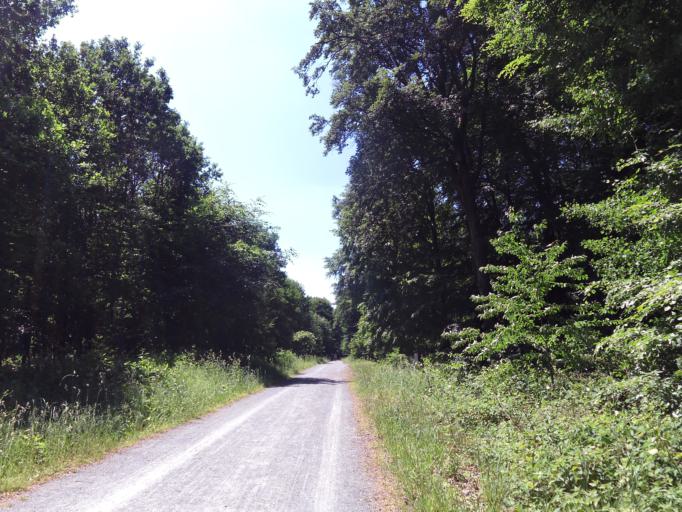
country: DE
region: Hesse
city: Langen
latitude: 50.0062
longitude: 8.6432
